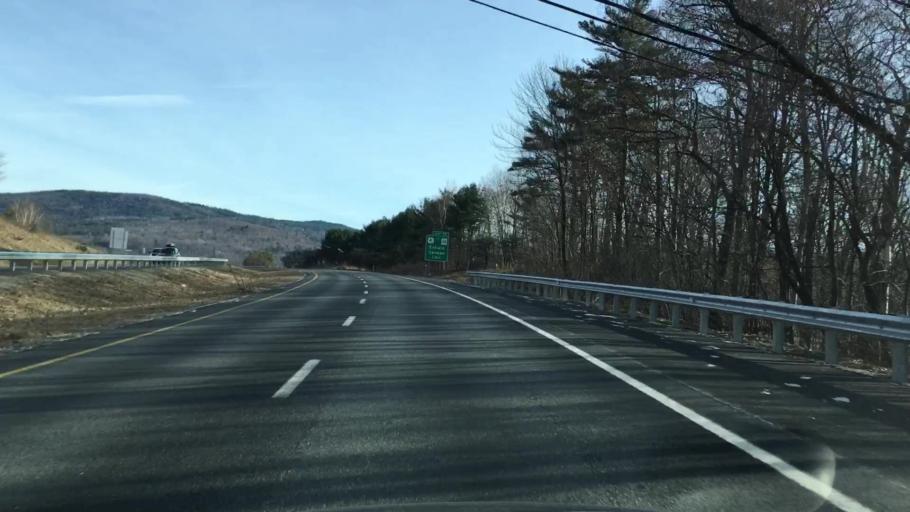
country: US
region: New Hampshire
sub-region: Grafton County
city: Lebanon
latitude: 43.6419
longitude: -72.2281
